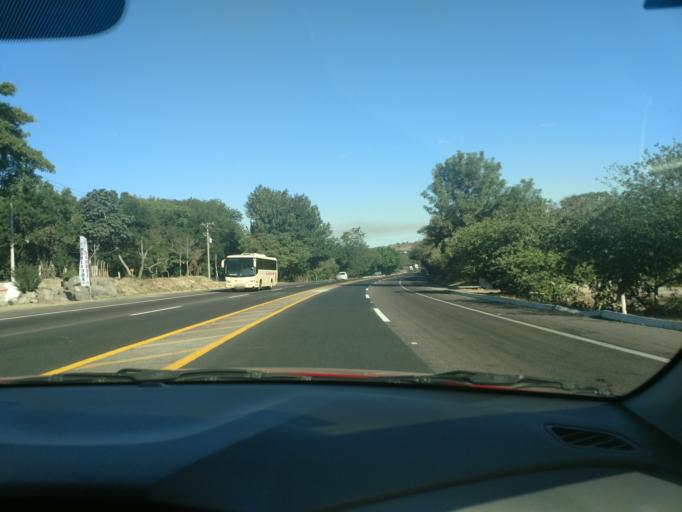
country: MX
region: Nayarit
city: Tepic
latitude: 21.5356
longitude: -104.9402
